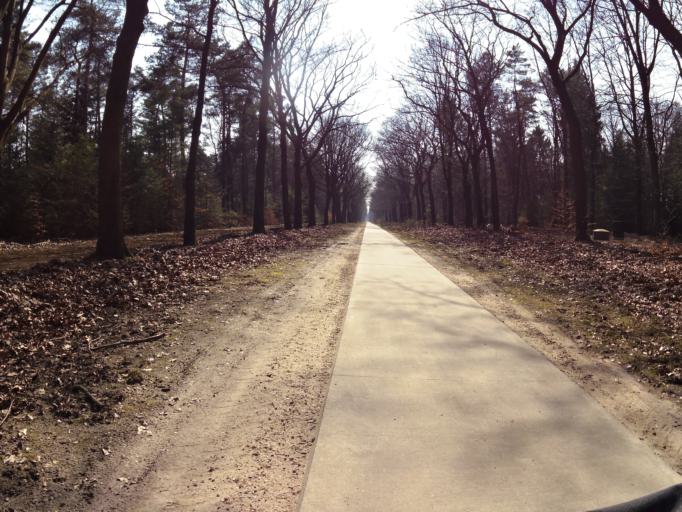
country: NL
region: Gelderland
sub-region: Gemeente Epe
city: Epe
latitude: 52.3771
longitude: 5.9642
